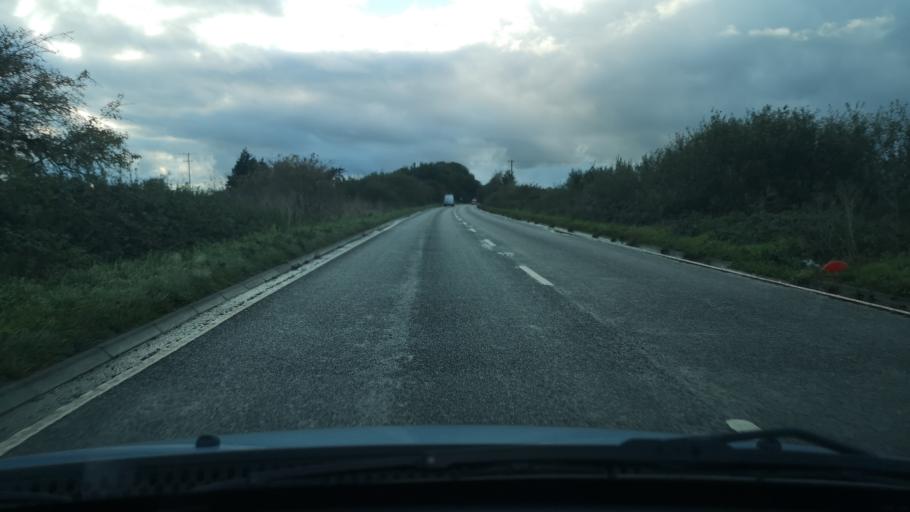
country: GB
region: England
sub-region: North Lincolnshire
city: Crowle
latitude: 53.5798
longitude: -0.8757
